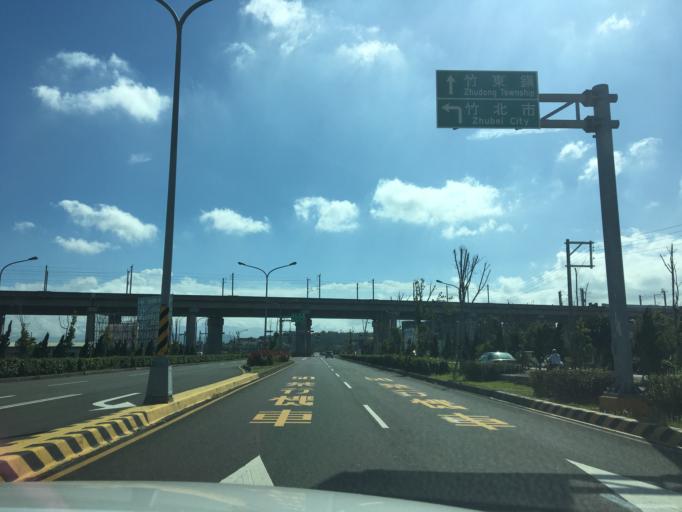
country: TW
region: Taiwan
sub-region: Hsinchu
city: Zhubei
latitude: 24.7862
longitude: 121.0331
